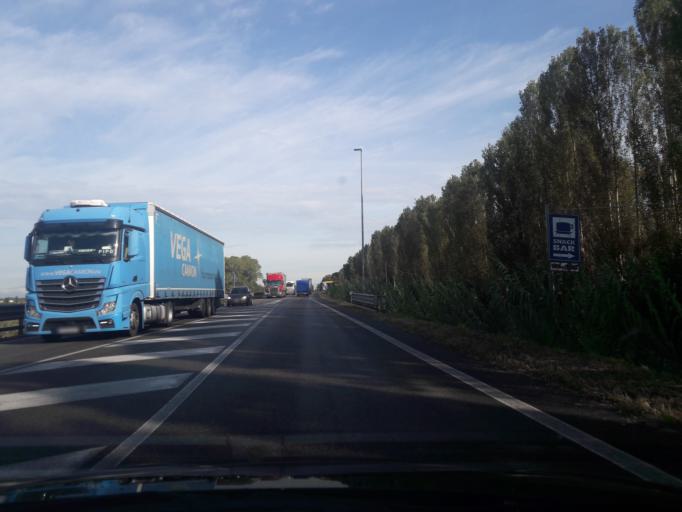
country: IT
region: Veneto
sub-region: Provincia di Venezia
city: Campagna Lupia
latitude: 45.3291
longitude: 12.1342
